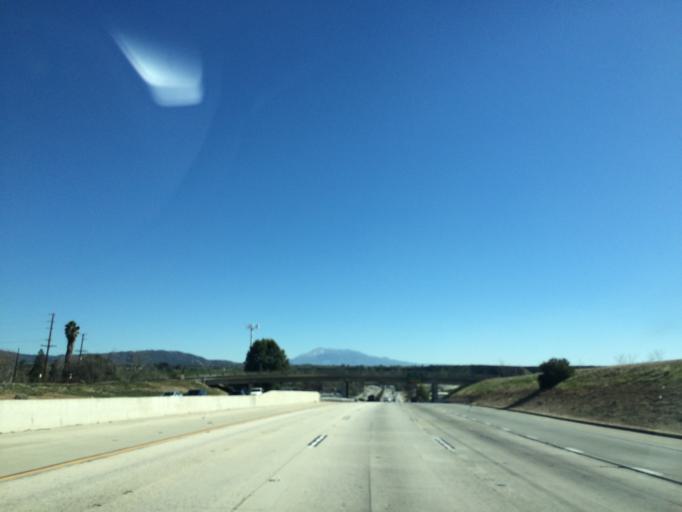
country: US
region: California
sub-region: Riverside County
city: Calimesa
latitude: 34.0228
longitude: -117.1060
